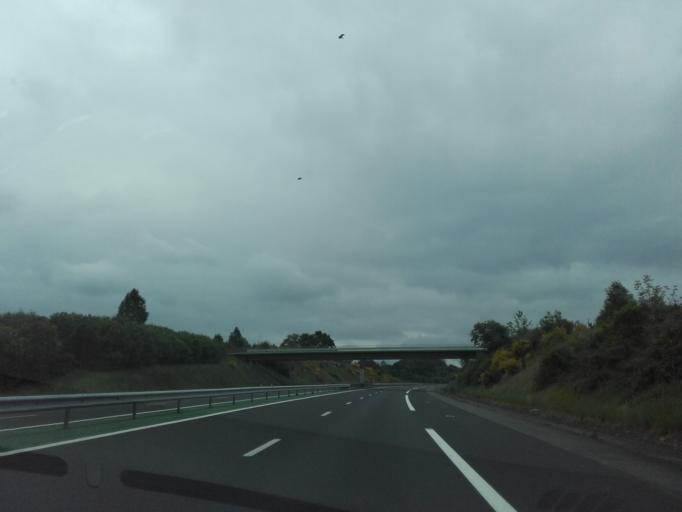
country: FR
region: Limousin
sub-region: Departement de la Correze
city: Saint-Mexant
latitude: 45.3074
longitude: 1.6703
